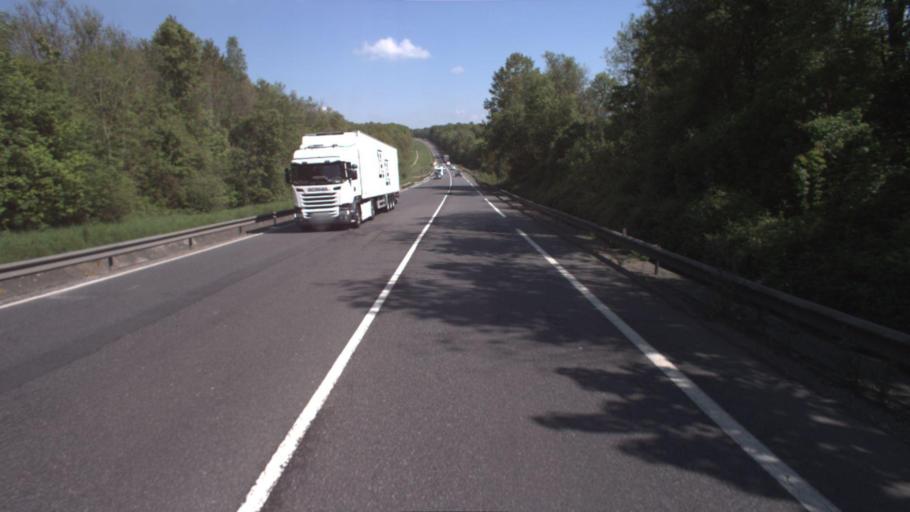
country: FR
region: Ile-de-France
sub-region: Departement de Seine-et-Marne
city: Guignes
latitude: 48.6568
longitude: 2.8072
